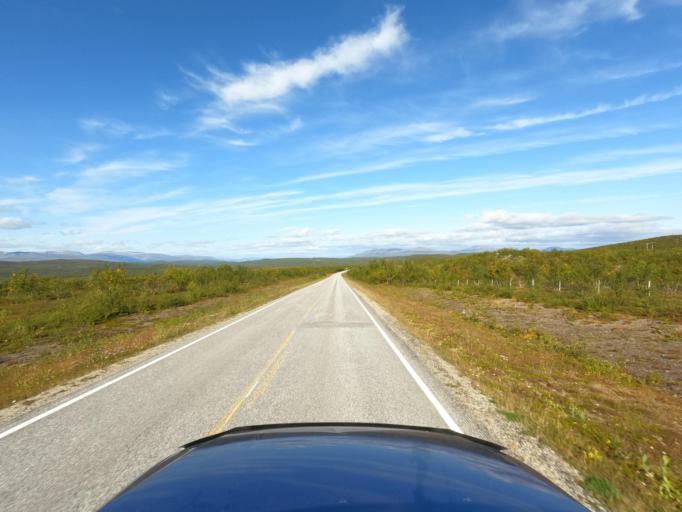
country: NO
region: Finnmark Fylke
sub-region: Karasjok
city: Karasjohka
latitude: 69.7242
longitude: 25.2364
